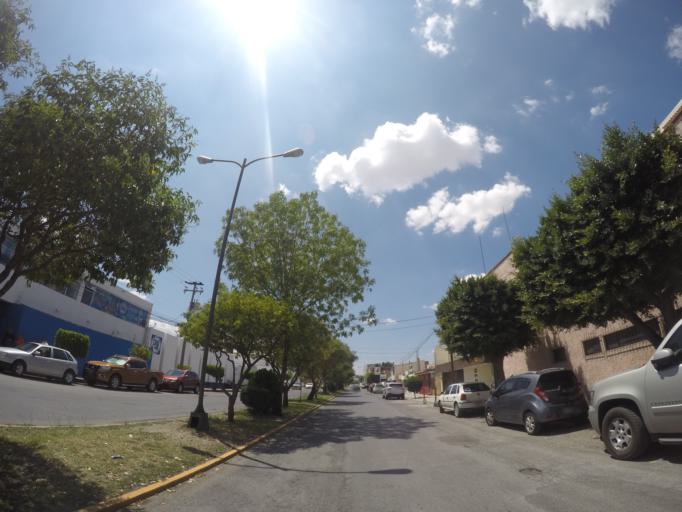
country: MX
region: San Luis Potosi
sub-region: San Luis Potosi
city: San Luis Potosi
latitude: 22.1438
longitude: -100.9877
